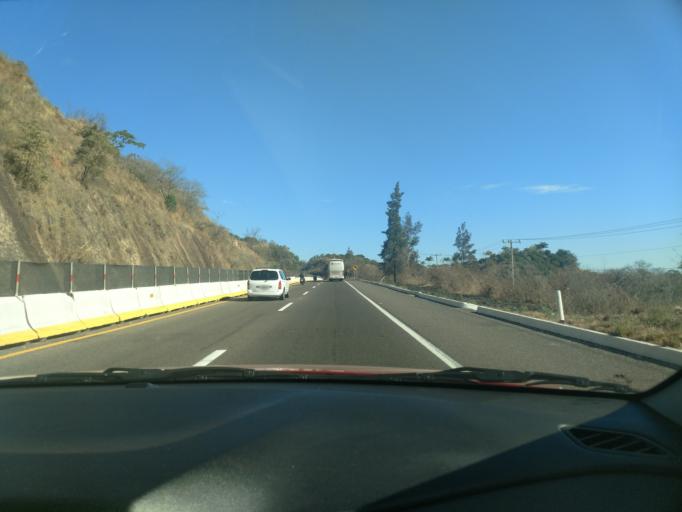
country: MX
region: Nayarit
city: Tepic
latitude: 21.5543
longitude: -104.9596
